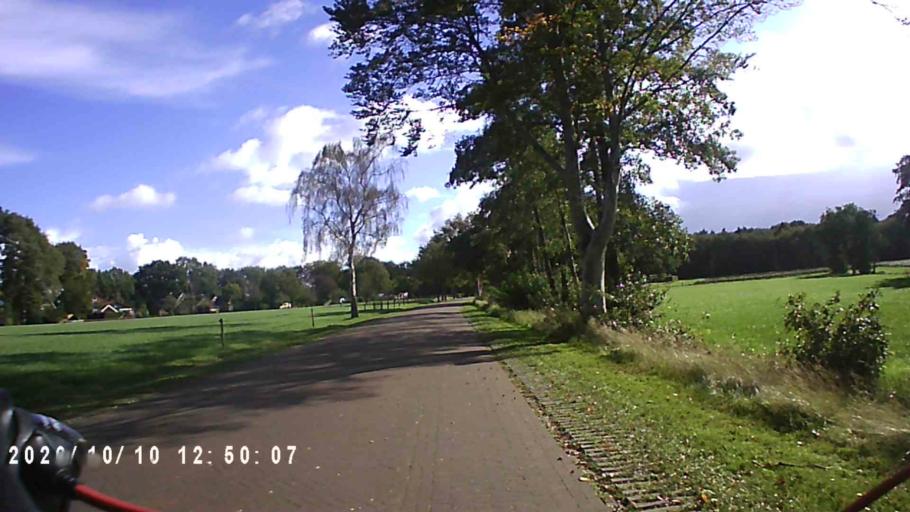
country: NL
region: Friesland
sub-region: Gemeente Weststellingwerf
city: Noordwolde
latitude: 52.9206
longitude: 6.2531
